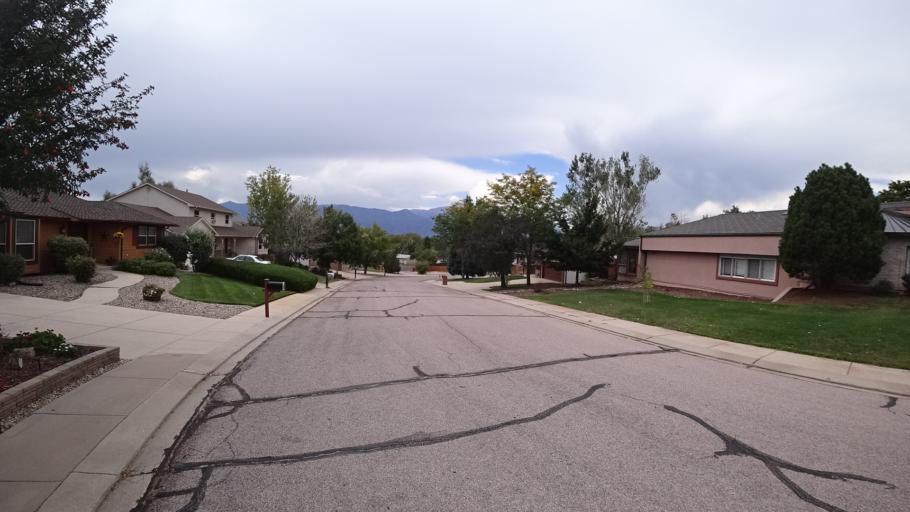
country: US
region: Colorado
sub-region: El Paso County
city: Colorado Springs
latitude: 38.8694
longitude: -104.7842
